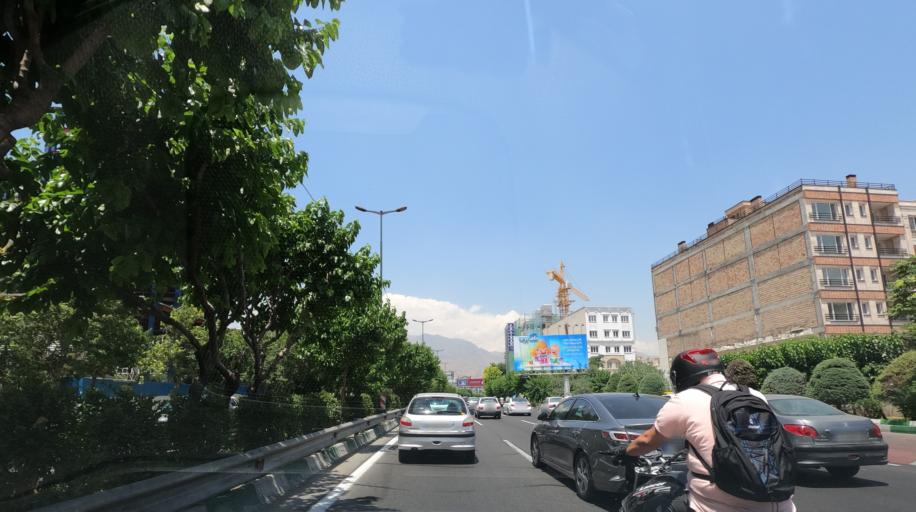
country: IR
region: Tehran
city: Tajrish
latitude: 35.7653
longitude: 51.4219
